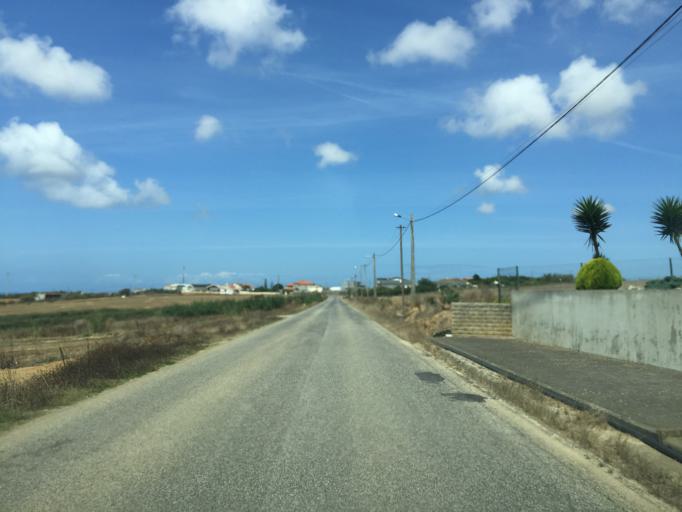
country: PT
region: Leiria
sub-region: Peniche
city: Atouguia da Baleia
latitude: 39.2894
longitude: -9.3068
